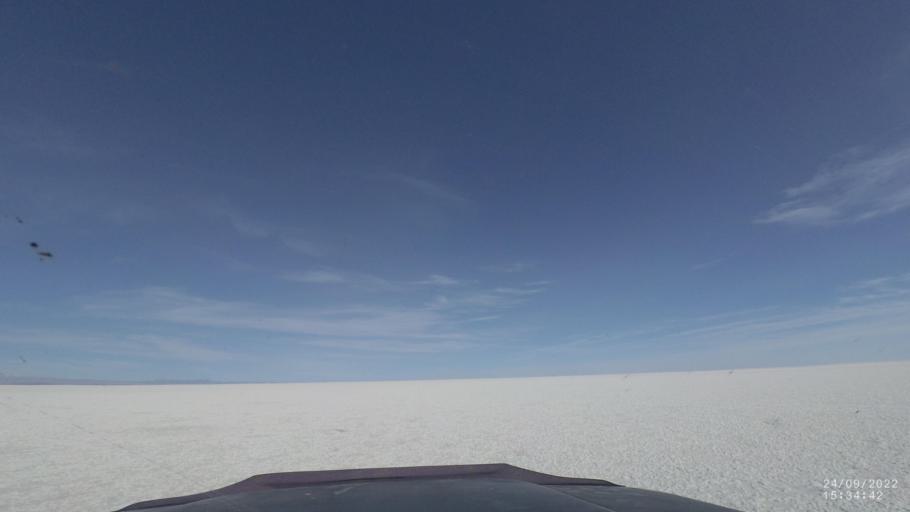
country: BO
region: Potosi
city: Colchani
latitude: -20.1272
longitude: -67.2602
